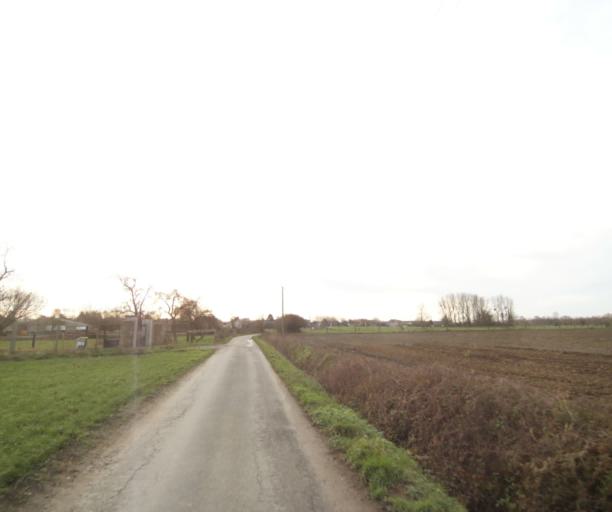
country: BE
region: Wallonia
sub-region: Province du Hainaut
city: Peruwelz
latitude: 50.4927
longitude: 3.5771
